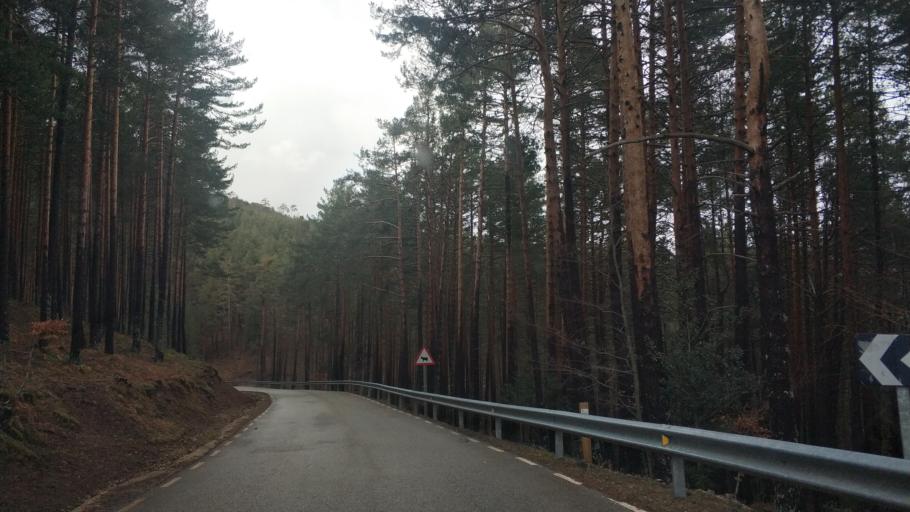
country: ES
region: Castille and Leon
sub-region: Provincia de Burgos
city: Neila
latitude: 42.0473
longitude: -3.0105
